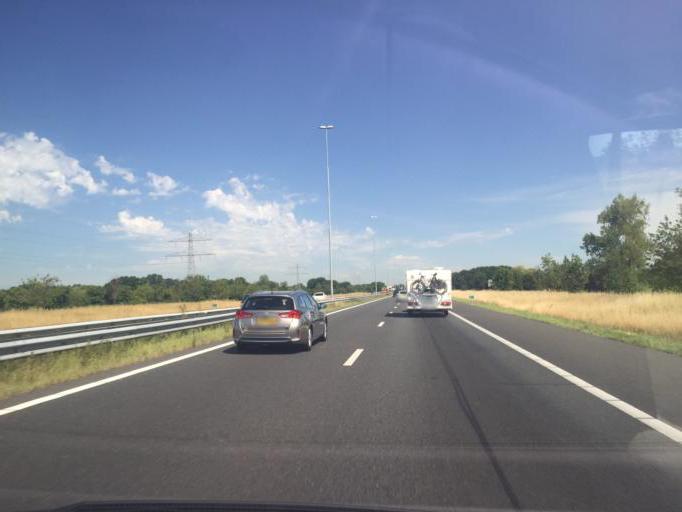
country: NL
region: North Brabant
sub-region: Gemeente Cuijk
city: Cuijk
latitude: 51.7447
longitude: 5.8417
